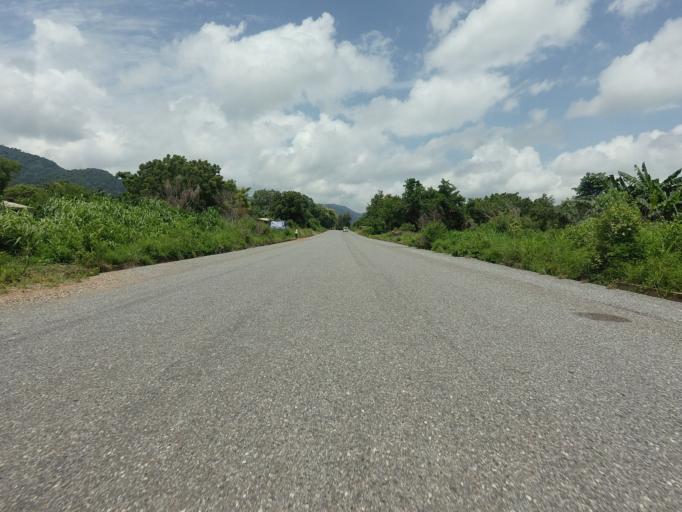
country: GH
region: Volta
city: Kpandu
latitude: 6.8519
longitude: 0.3934
